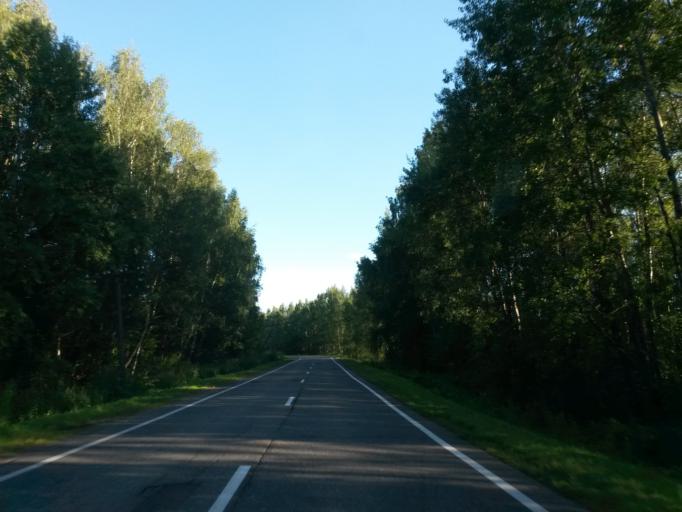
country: RU
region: Jaroslavl
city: Tutayev
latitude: 57.9151
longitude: 39.5155
